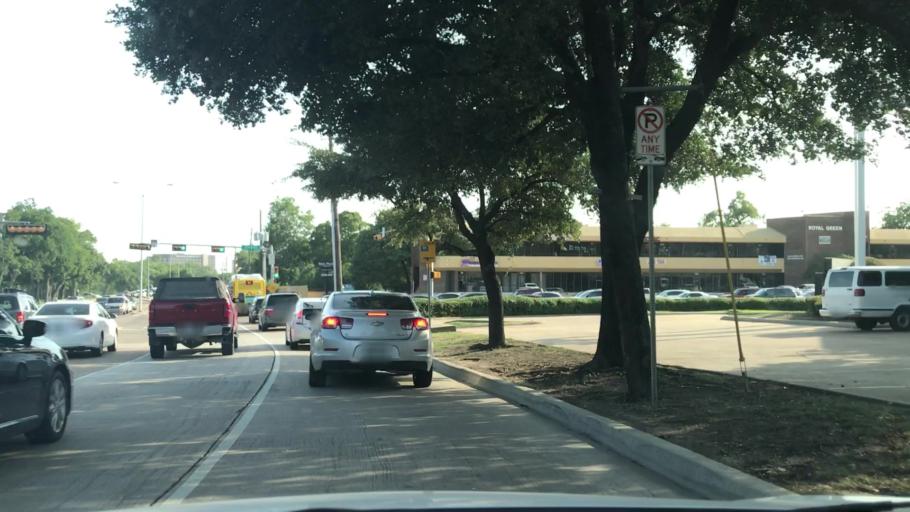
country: US
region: Texas
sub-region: Dallas County
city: Richardson
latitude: 32.8942
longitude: -96.7532
